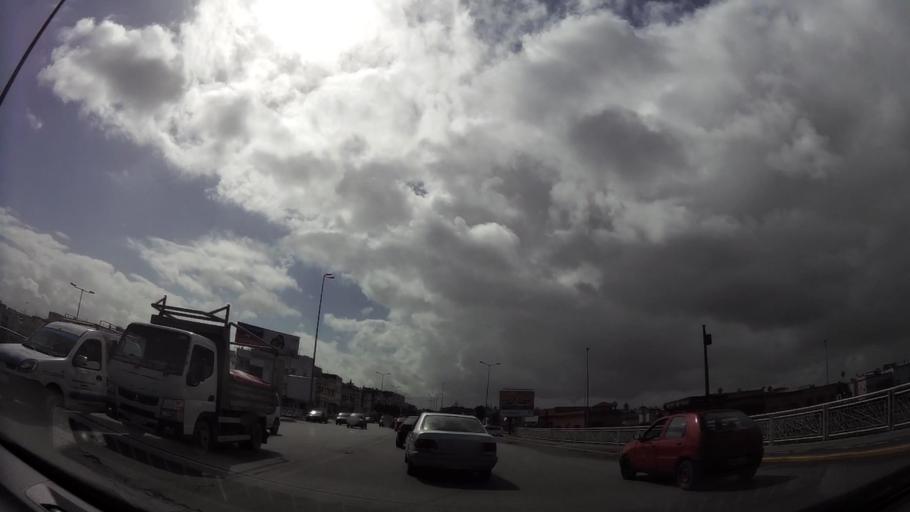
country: MA
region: Grand Casablanca
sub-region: Casablanca
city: Casablanca
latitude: 33.5572
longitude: -7.6067
